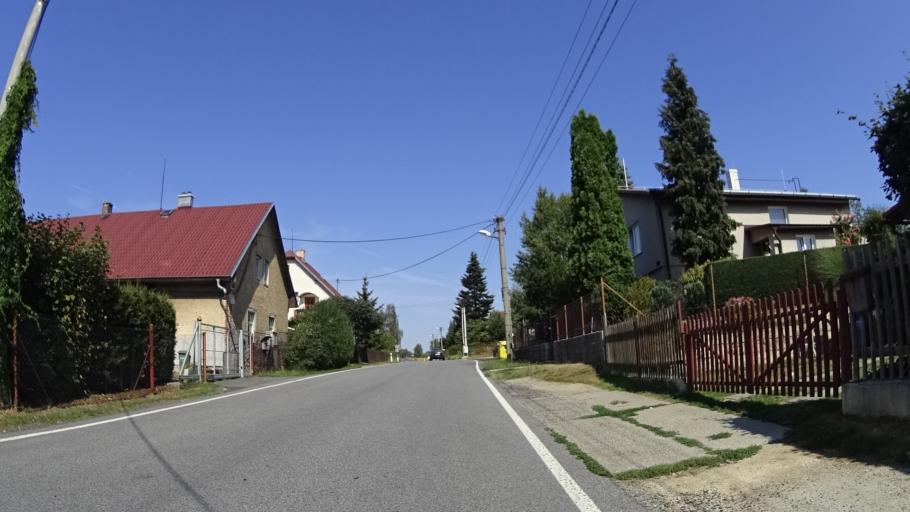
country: CZ
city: Chrastava
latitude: 50.7952
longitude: 14.9899
